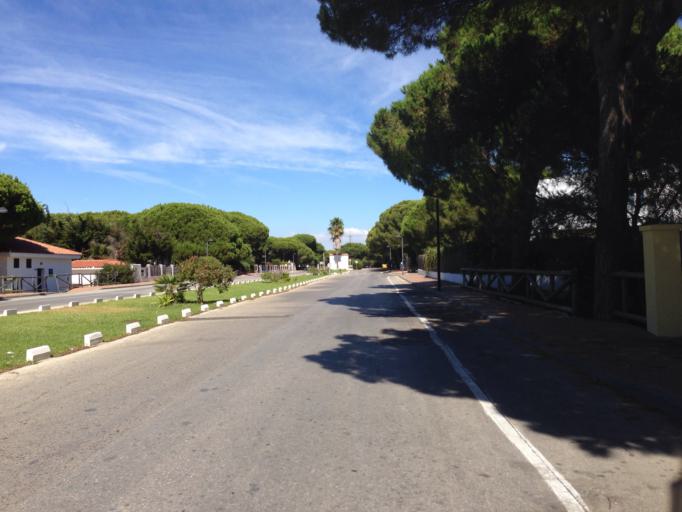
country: ES
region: Andalusia
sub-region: Provincia de Cadiz
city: Conil de la Frontera
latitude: 36.3182
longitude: -6.1416
